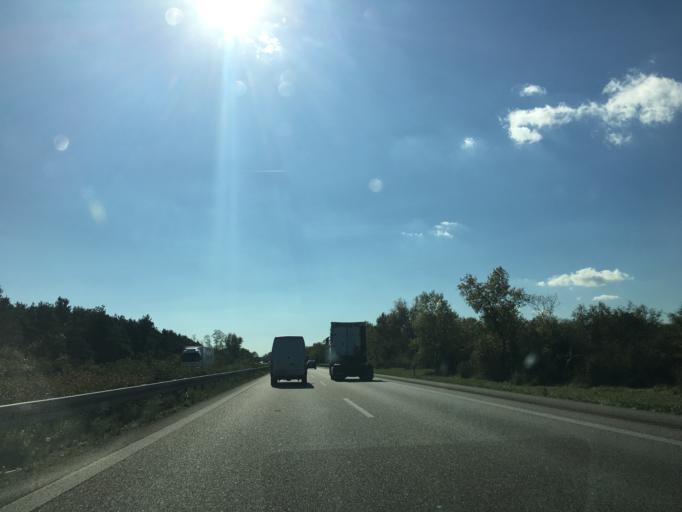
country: FR
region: Alsace
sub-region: Departement du Haut-Rhin
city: Chalampe
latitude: 47.7957
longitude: 7.5410
